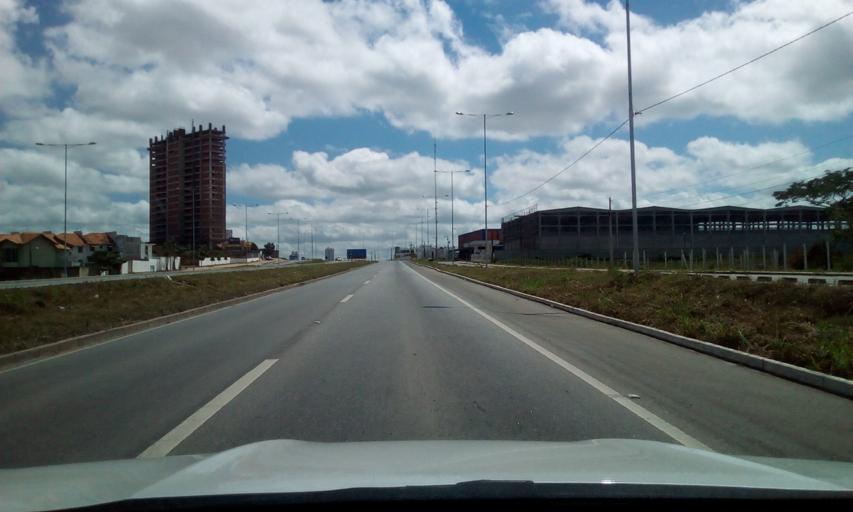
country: BR
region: Paraiba
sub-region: Campina Grande
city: Campina Grande
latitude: -7.2537
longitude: -35.8739
